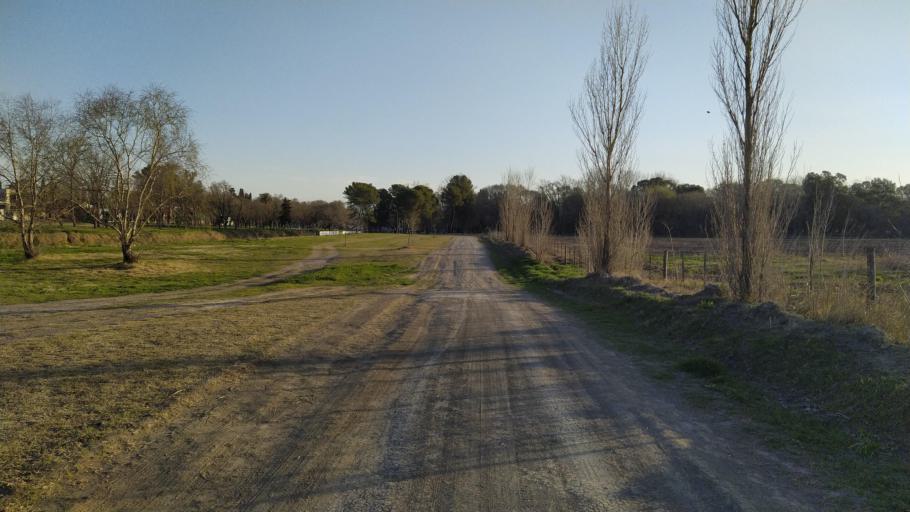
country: AR
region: Buenos Aires
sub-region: Partido de Salto
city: Salto
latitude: -34.2804
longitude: -60.2533
